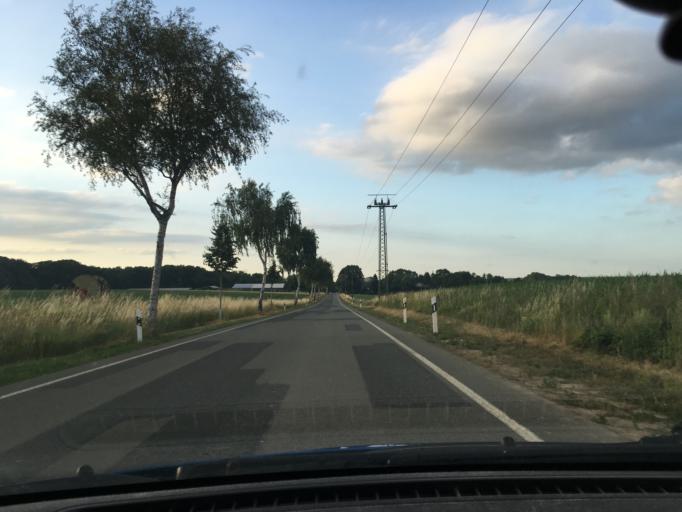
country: DE
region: Lower Saxony
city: Eyendorf
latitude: 53.1877
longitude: 10.1875
